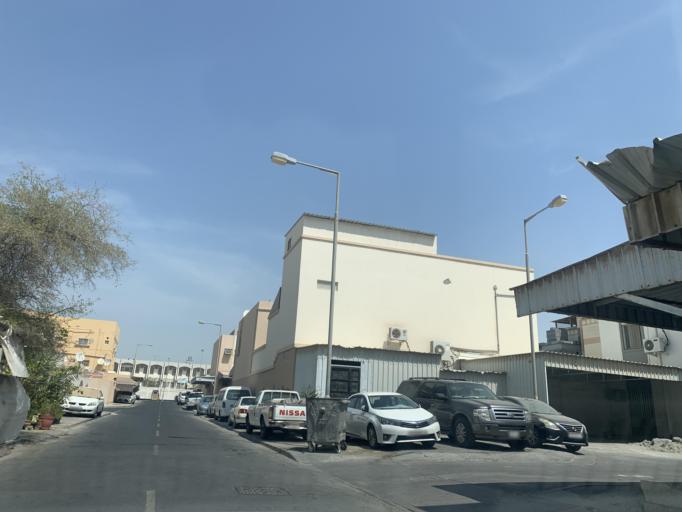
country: BH
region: Central Governorate
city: Madinat Hamad
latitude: 26.1347
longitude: 50.5026
